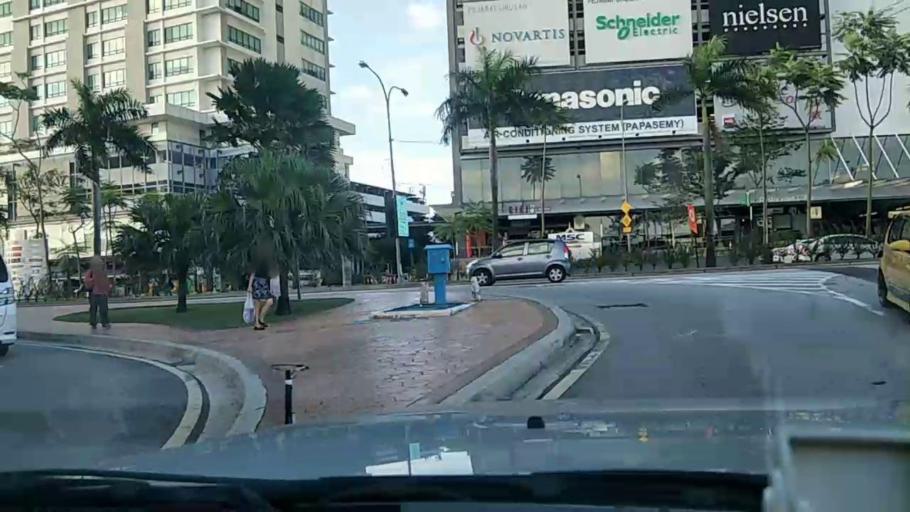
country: MY
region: Selangor
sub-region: Petaling
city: Petaling Jaya
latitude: 3.1092
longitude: 101.6376
